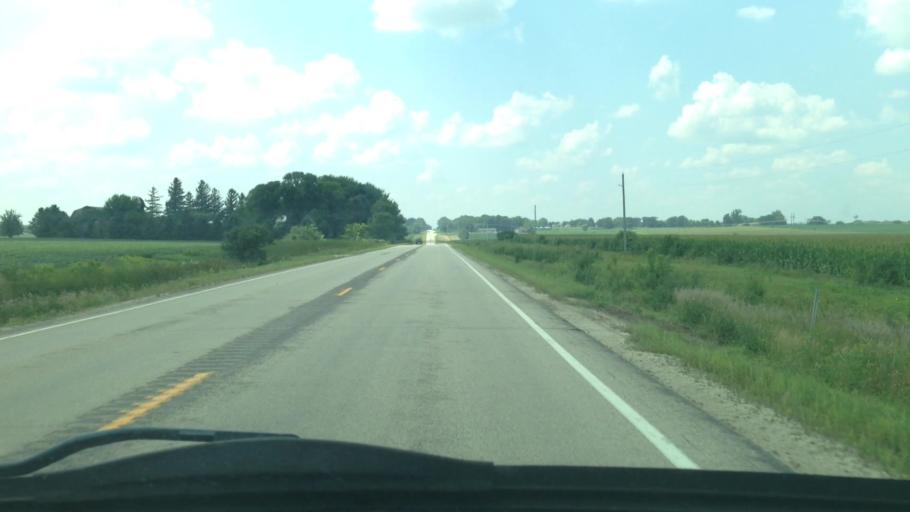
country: US
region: Minnesota
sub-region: Olmsted County
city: Stewartville
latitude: 43.8556
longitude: -92.4525
